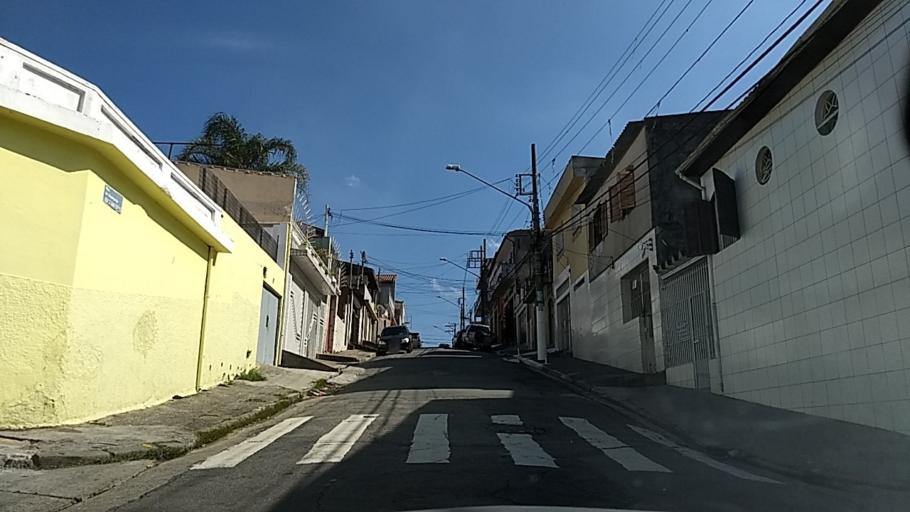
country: BR
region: Sao Paulo
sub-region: Guarulhos
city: Guarulhos
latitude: -23.4830
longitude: -46.5922
